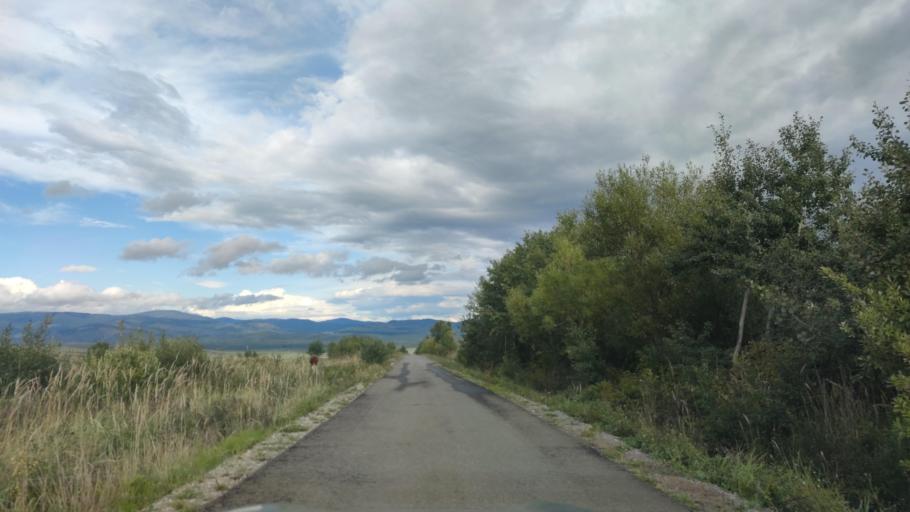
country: RO
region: Harghita
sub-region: Comuna Remetea
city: Remetea
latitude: 46.8158
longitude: 25.3865
